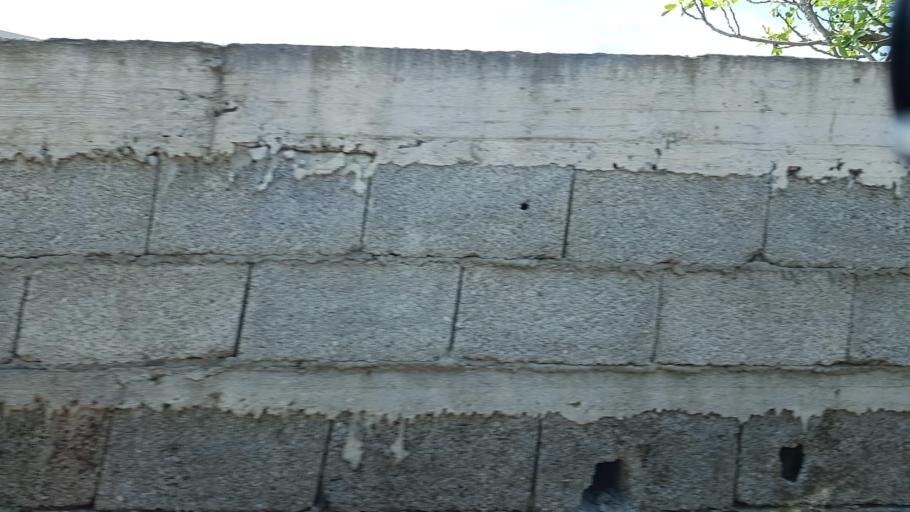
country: AL
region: Shkoder
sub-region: Rrethi i Malesia e Madhe
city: Gruemire
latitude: 42.1347
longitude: 19.5495
